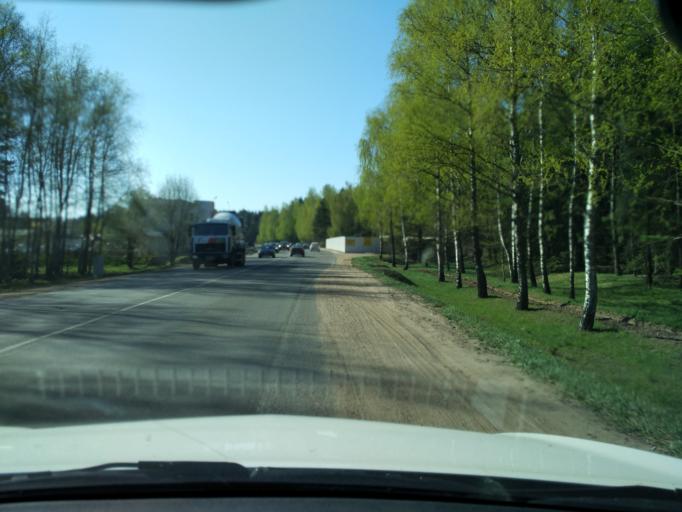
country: BY
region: Minsk
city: Lyeskawka
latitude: 53.9584
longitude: 27.7237
